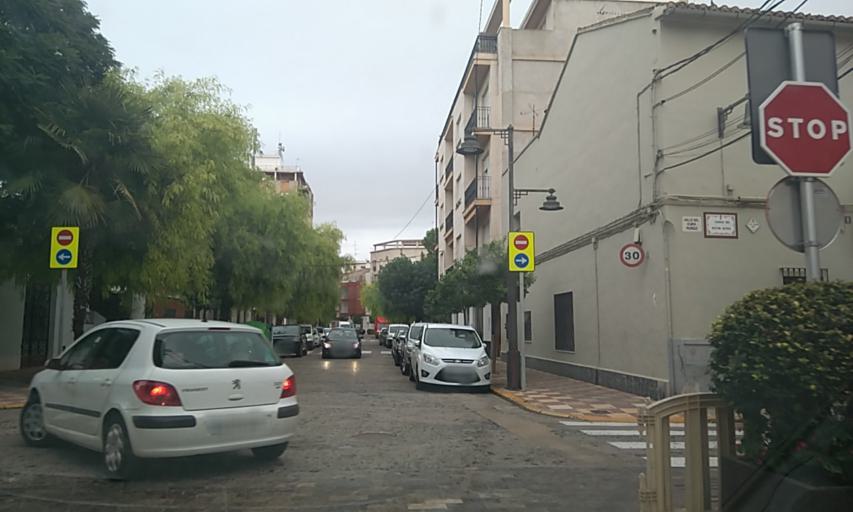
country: ES
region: Valencia
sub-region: Provincia de Valencia
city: L'Alcudia
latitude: 39.1971
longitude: -0.5065
